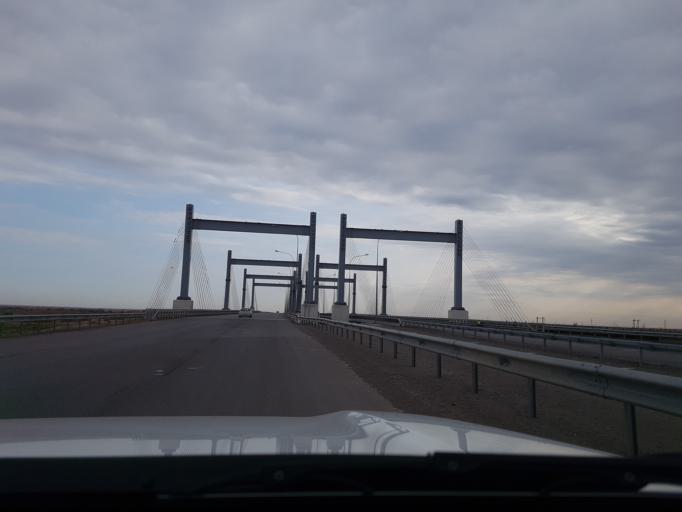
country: TM
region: Ahal
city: Tejen
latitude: 37.2313
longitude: 60.1493
